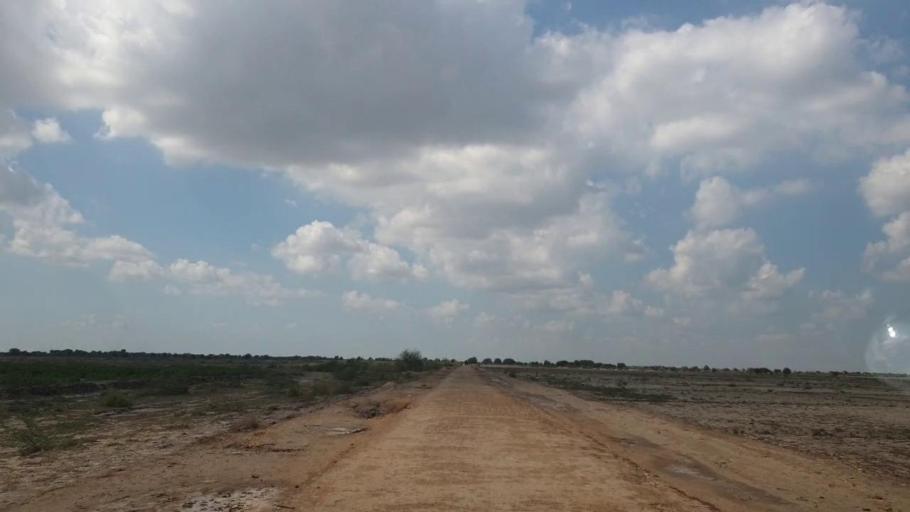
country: PK
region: Sindh
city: Pithoro
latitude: 25.5987
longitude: 69.3590
